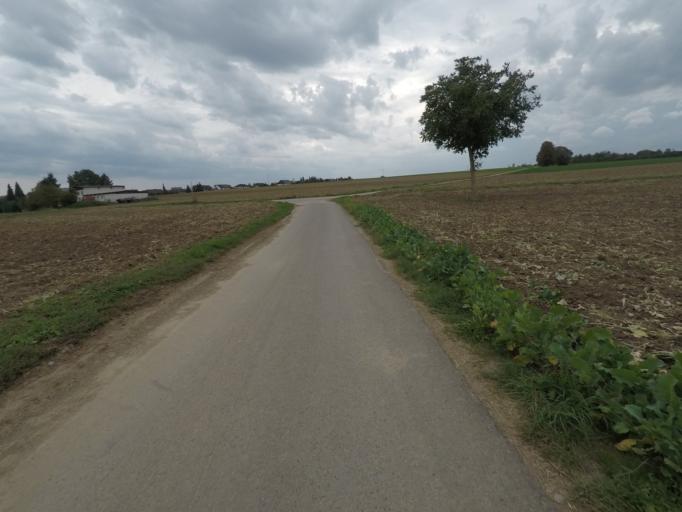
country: DE
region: Baden-Wuerttemberg
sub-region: Regierungsbezirk Stuttgart
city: Herrenberg
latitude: 48.5631
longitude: 8.8991
